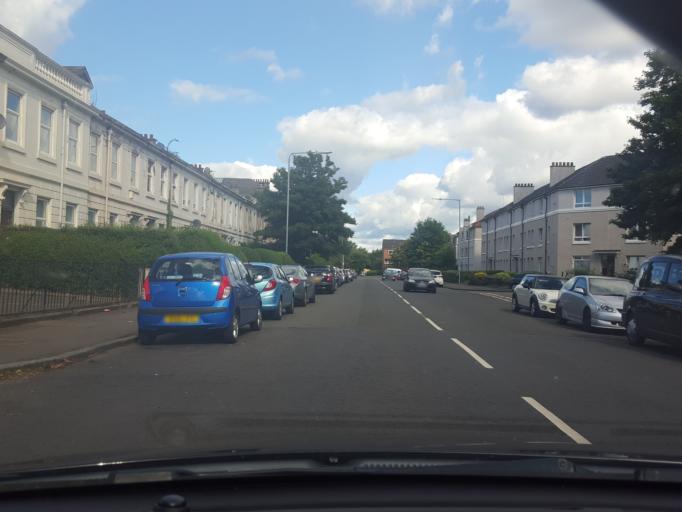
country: GB
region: Scotland
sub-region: Glasgow City
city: Glasgow
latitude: 55.8554
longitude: -4.3039
